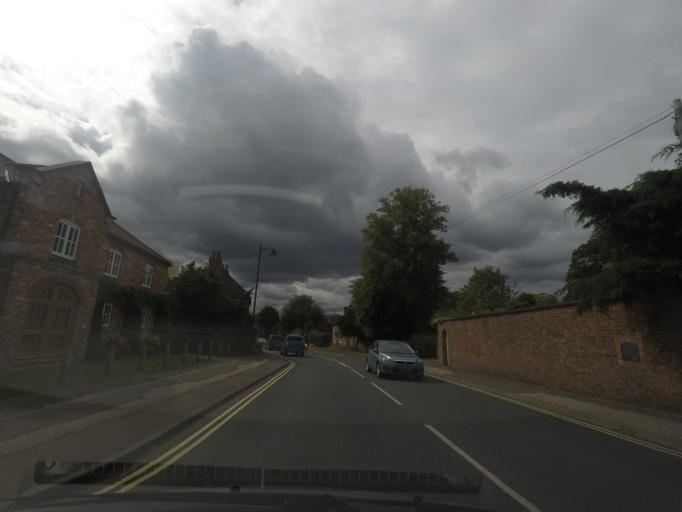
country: GB
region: England
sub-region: City of York
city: Heslington
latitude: 53.9450
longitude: -1.0487
